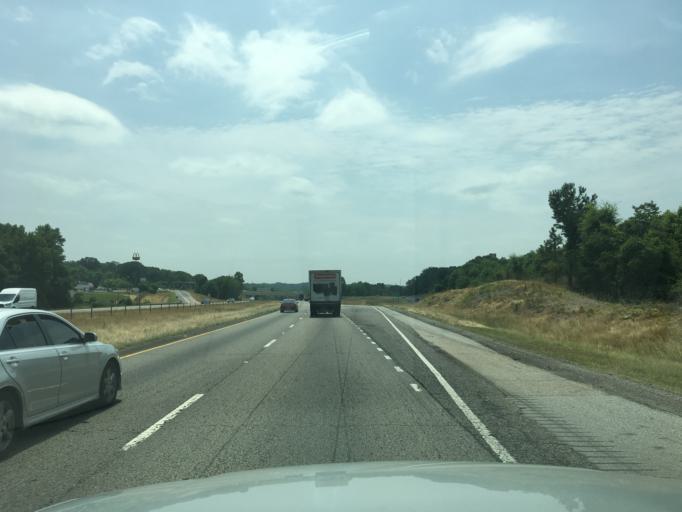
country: US
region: Georgia
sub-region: Jackson County
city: Jefferson
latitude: 34.1561
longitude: -83.6420
